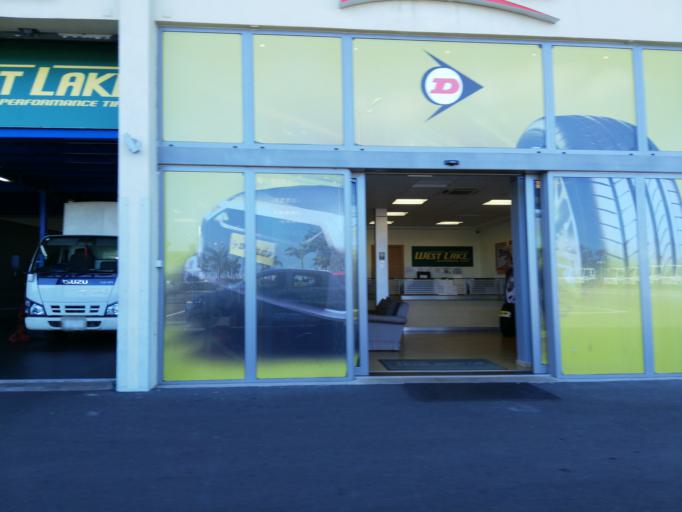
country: MU
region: Moka
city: Moka
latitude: -20.2277
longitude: 57.4922
